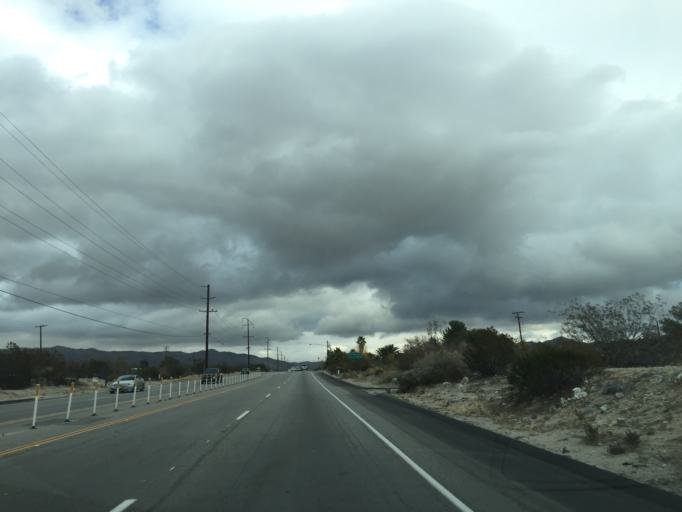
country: US
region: California
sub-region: San Bernardino County
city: Morongo Valley
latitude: 34.0645
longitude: -116.5584
